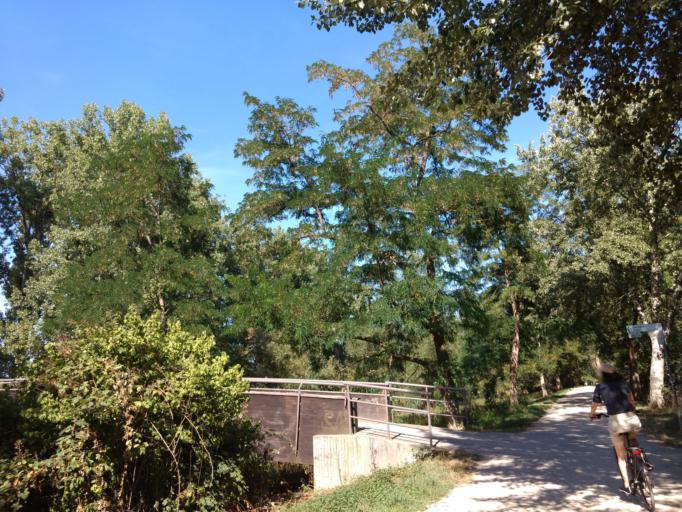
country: DE
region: Rheinland-Pfalz
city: Sinzig
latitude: 50.5509
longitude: 7.2496
